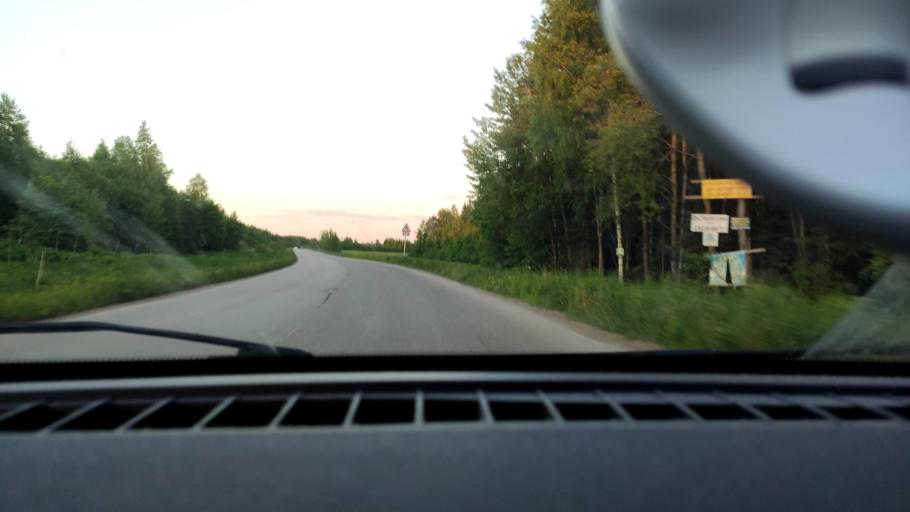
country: RU
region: Perm
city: Polazna
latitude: 58.2103
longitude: 56.4483
